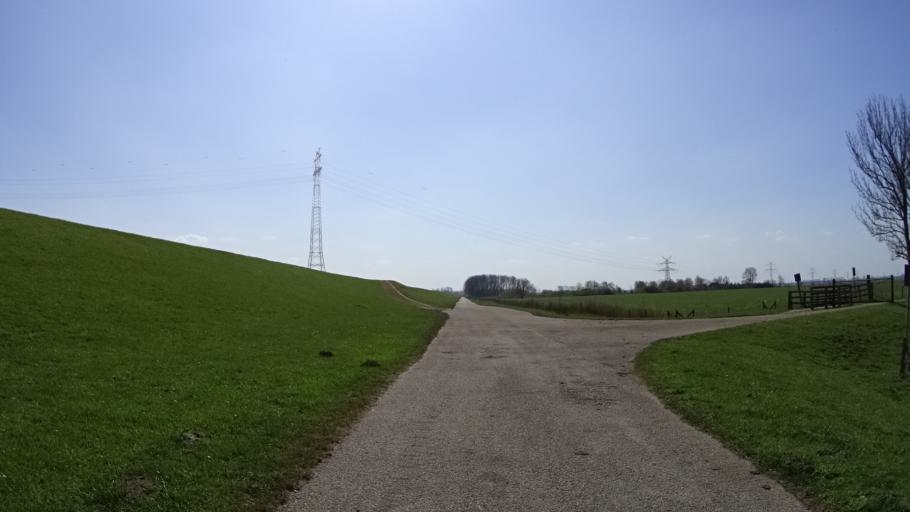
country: DE
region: Lower Saxony
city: Weener
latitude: 53.1513
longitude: 7.3709
